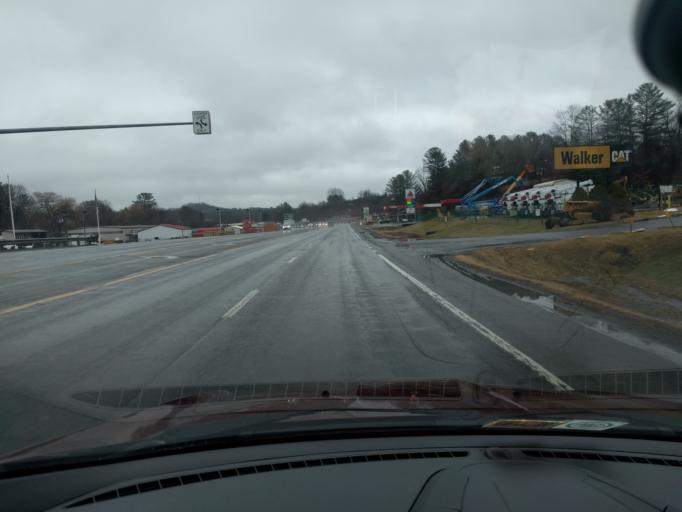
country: US
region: West Virginia
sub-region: Raleigh County
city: Crab Orchard
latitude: 37.7395
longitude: -81.2336
